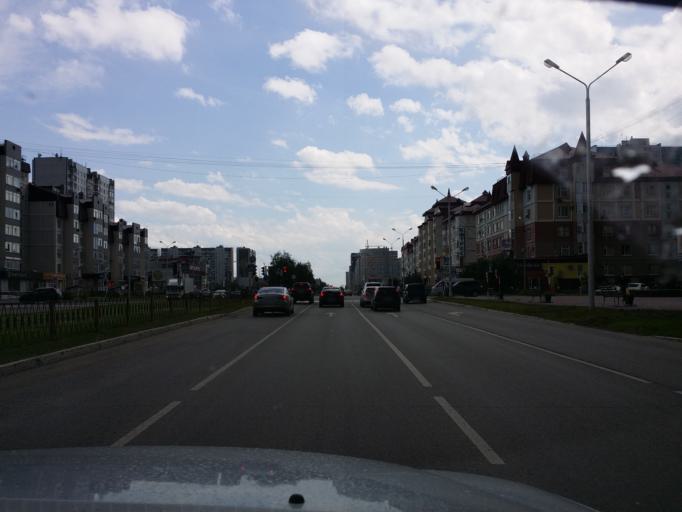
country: RU
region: Khanty-Mansiyskiy Avtonomnyy Okrug
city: Nizhnevartovsk
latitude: 60.9372
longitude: 76.5799
